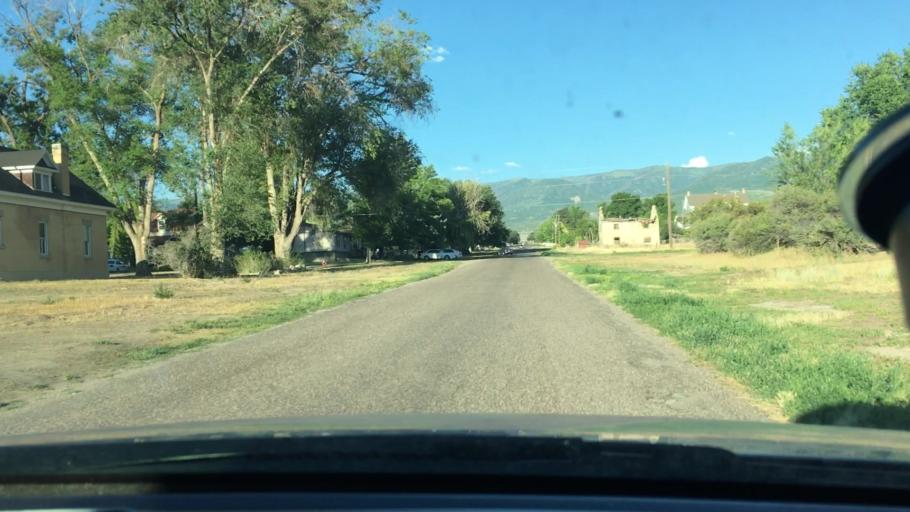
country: US
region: Utah
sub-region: Sanpete County
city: Mount Pleasant
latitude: 39.5409
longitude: -111.4600
